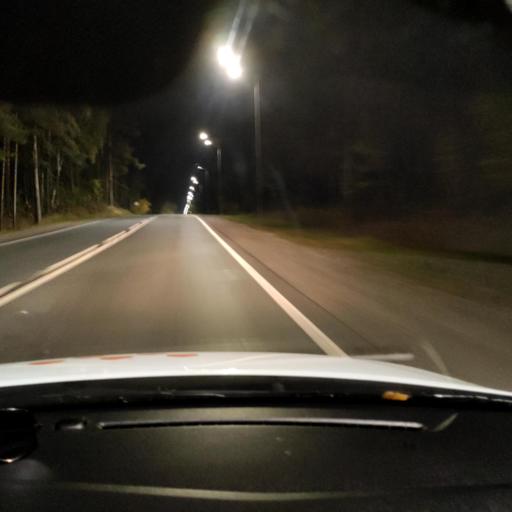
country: RU
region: Tatarstan
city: Verkhniy Uslon
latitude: 55.6384
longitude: 49.0410
